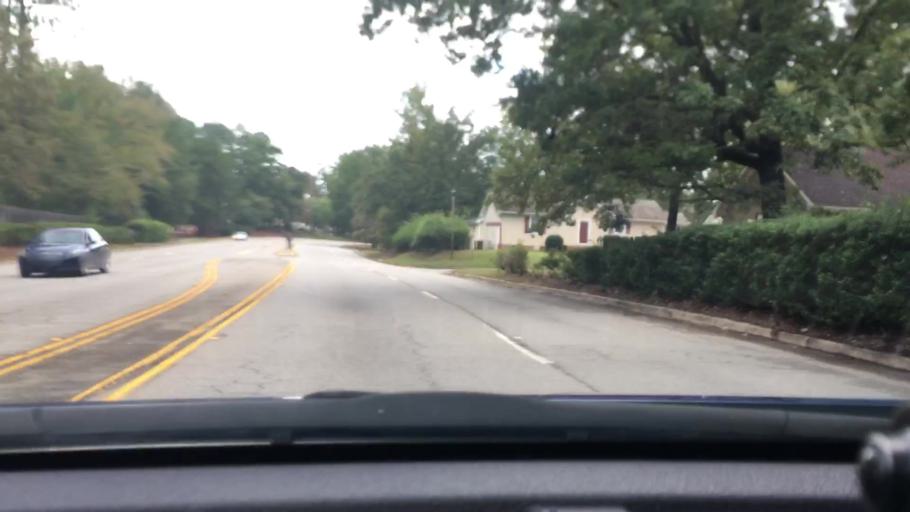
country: US
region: South Carolina
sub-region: Lexington County
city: Seven Oaks
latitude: 34.0833
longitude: -81.1441
